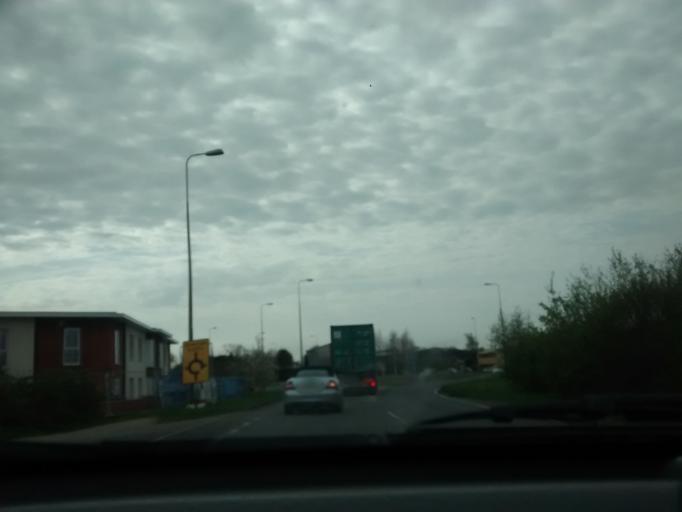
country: GB
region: England
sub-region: Oxfordshire
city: Bicester
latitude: 51.9065
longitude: -1.1297
